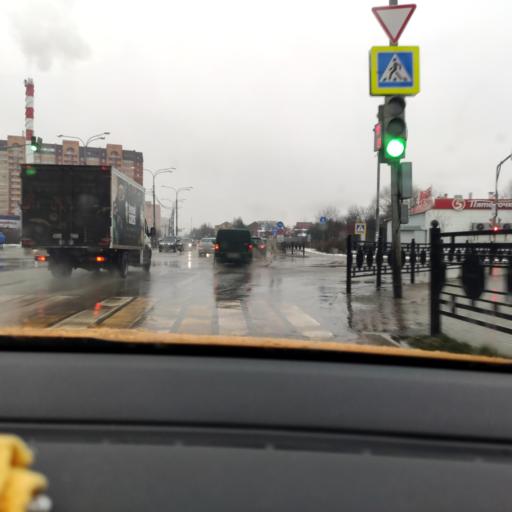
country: RU
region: Moskovskaya
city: Domodedovo
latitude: 55.4308
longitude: 37.7531
